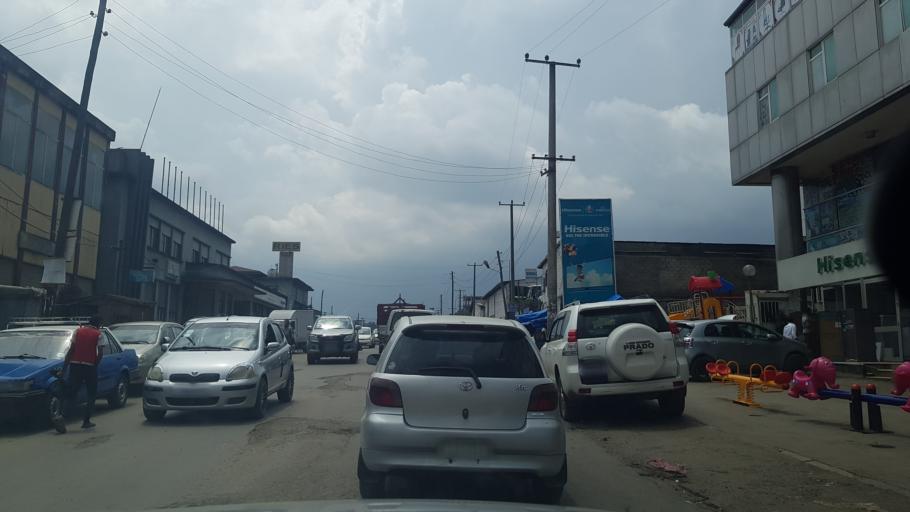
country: ET
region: Adis Abeba
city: Addis Ababa
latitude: 9.0324
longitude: 38.7468
